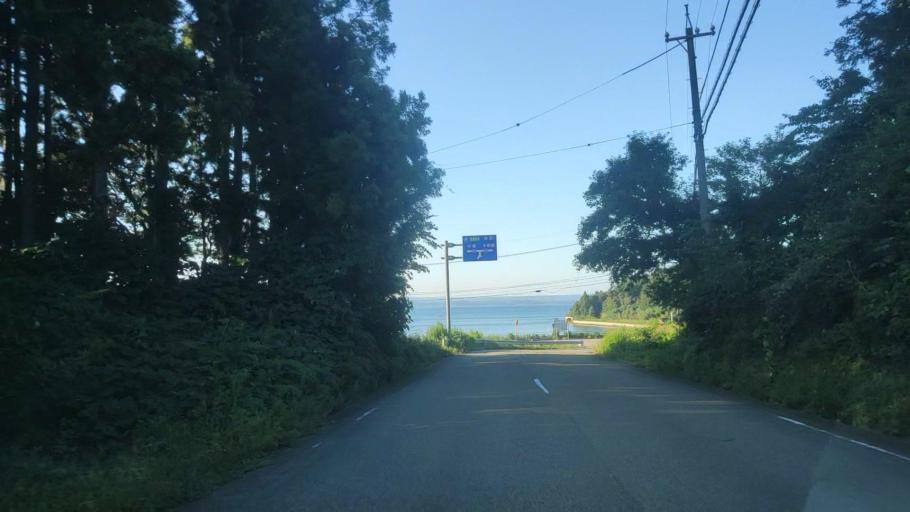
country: JP
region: Ishikawa
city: Nanao
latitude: 37.1317
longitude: 136.9311
